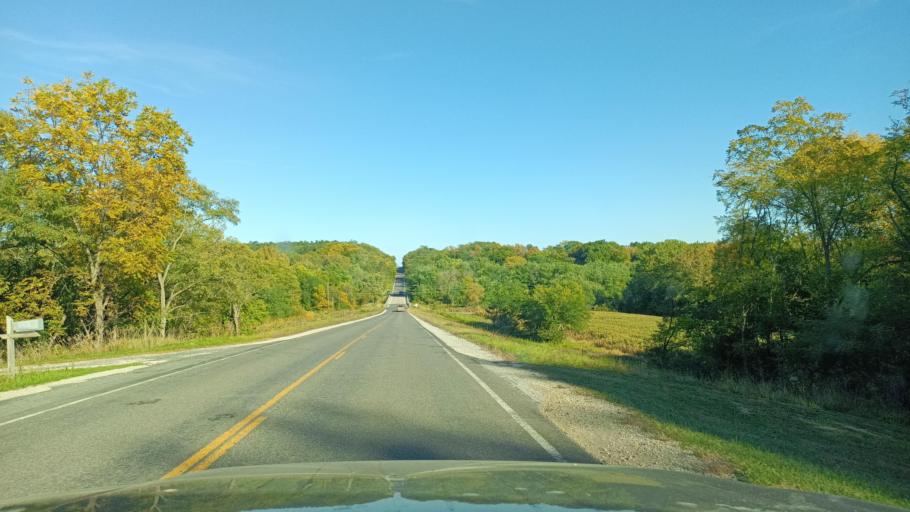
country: US
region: Illinois
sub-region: McLean County
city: Le Roy
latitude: 40.2245
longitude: -88.8249
